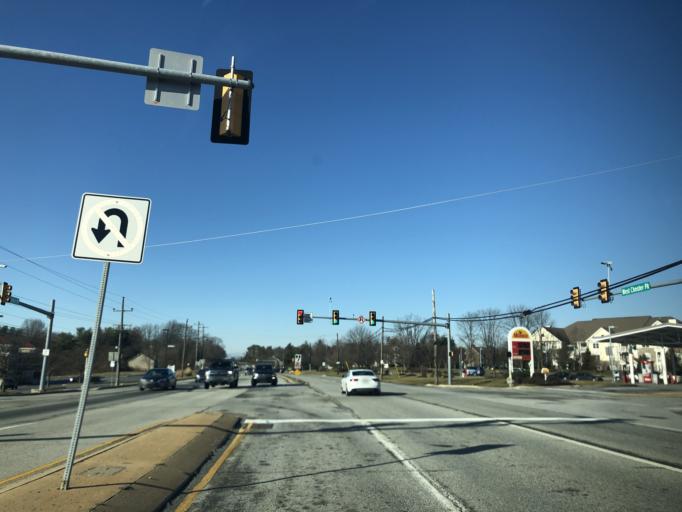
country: US
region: Pennsylvania
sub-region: Chester County
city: Malvern
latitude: 39.9668
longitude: -75.5265
